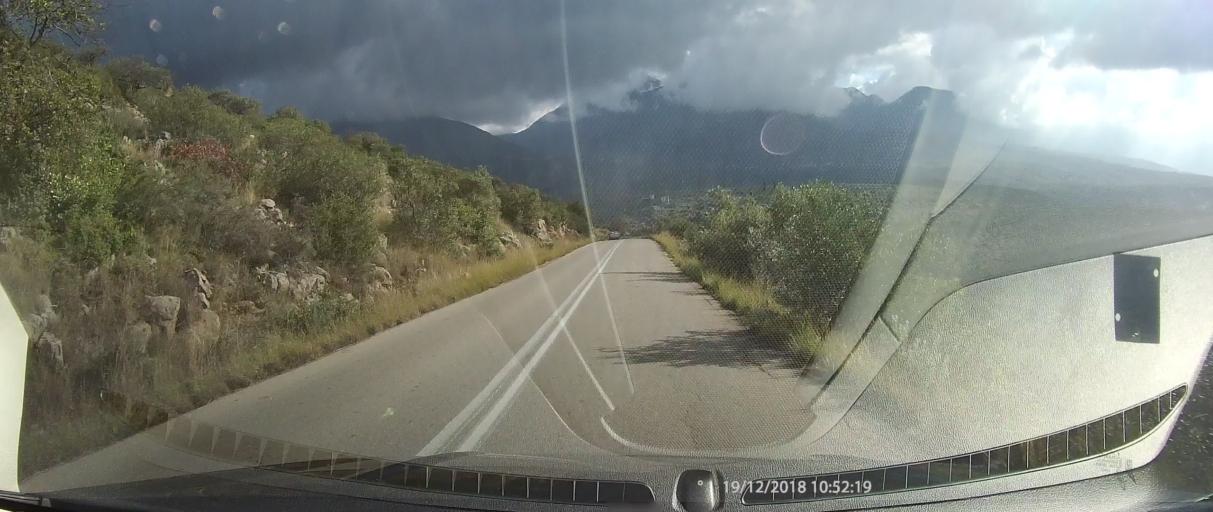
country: GR
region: Peloponnese
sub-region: Nomos Messinias
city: Kardamyli
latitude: 36.9136
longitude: 22.2257
